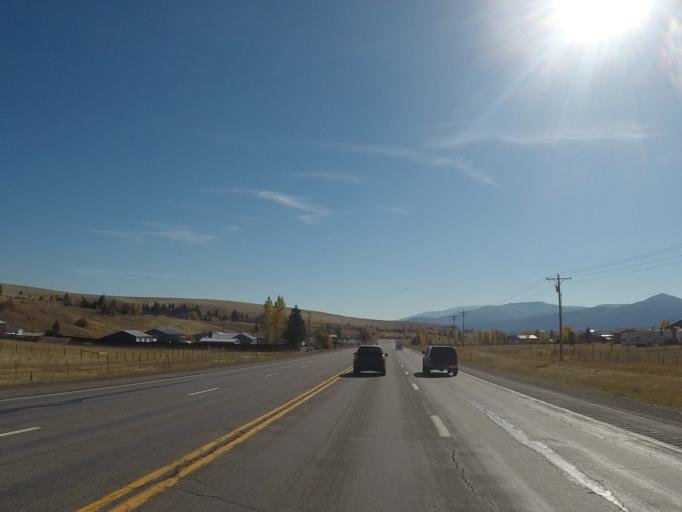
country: US
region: Montana
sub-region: Missoula County
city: Frenchtown
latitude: 46.9887
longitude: -114.1242
